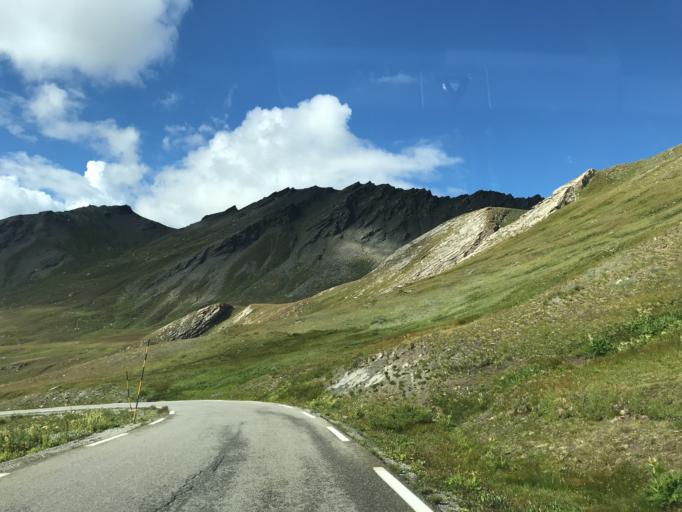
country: IT
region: Piedmont
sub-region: Provincia di Cuneo
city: Pontechianale
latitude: 44.6875
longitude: 6.9788
